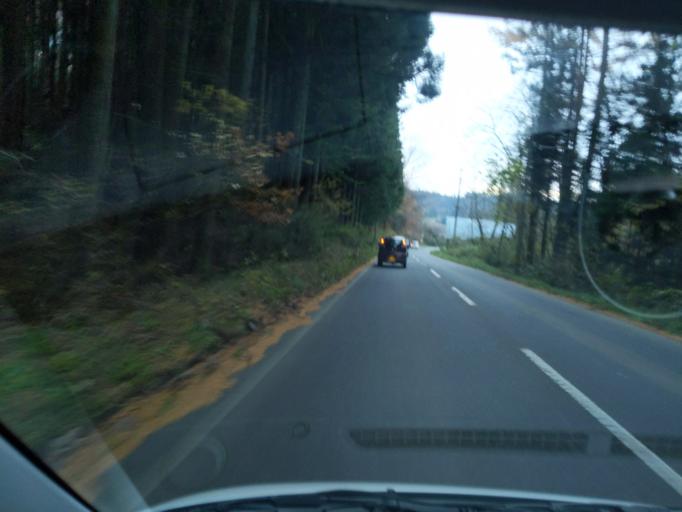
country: JP
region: Iwate
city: Ichinoseki
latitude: 39.0248
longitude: 141.3324
